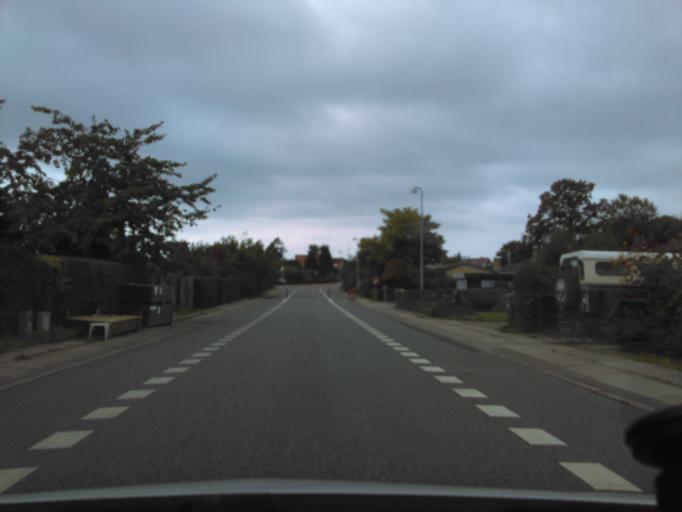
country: DK
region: Capital Region
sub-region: Fureso Kommune
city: Farum
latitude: 55.8111
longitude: 12.3461
